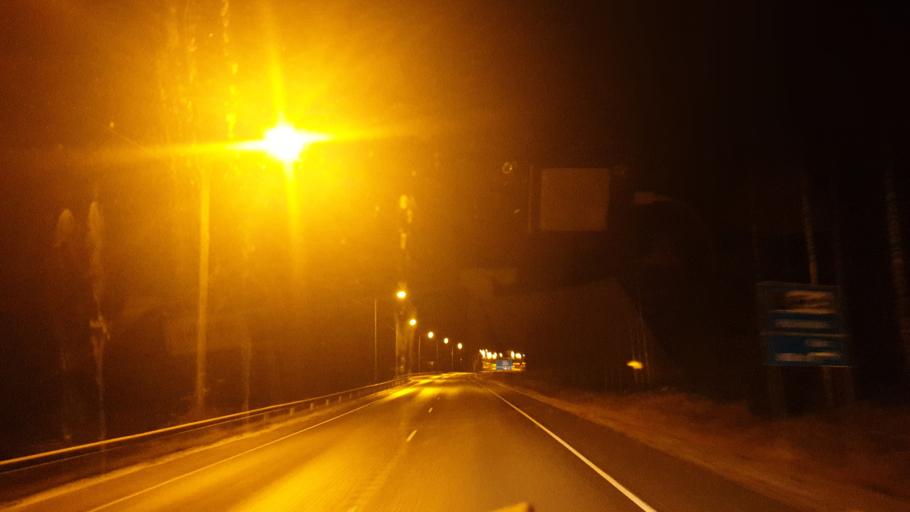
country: FI
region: Central Finland
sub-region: Jyvaeskylae
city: Toivakka
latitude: 62.2488
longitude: 26.1633
